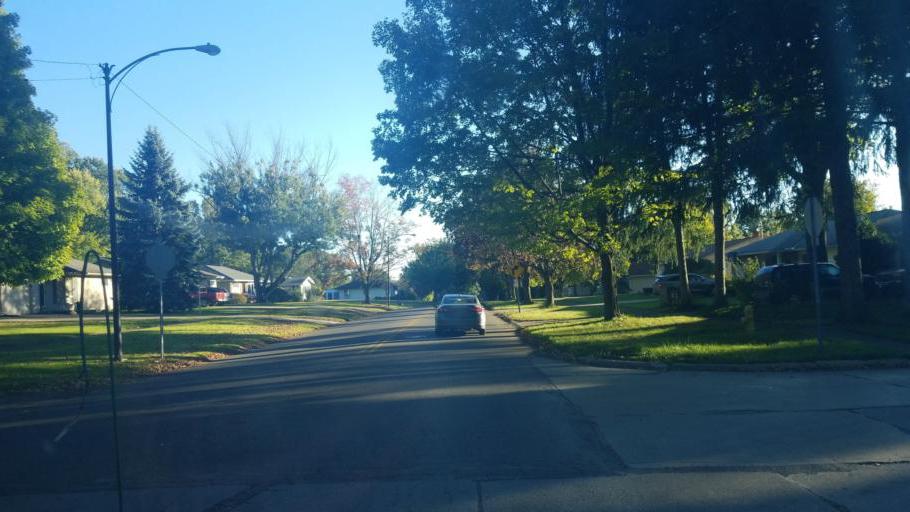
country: US
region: Ohio
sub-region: Columbiana County
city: Salem
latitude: 40.8936
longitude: -80.8332
